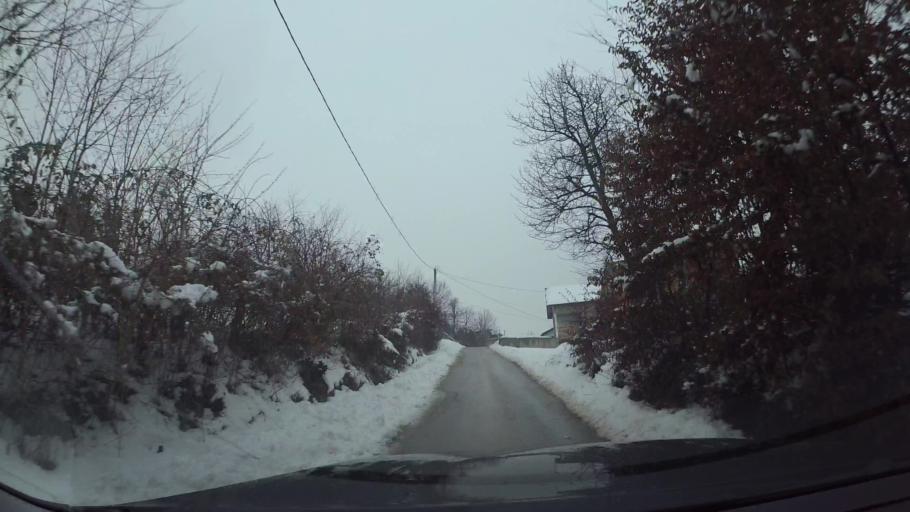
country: BA
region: Federation of Bosnia and Herzegovina
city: Hadzici
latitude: 43.8507
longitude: 18.2681
